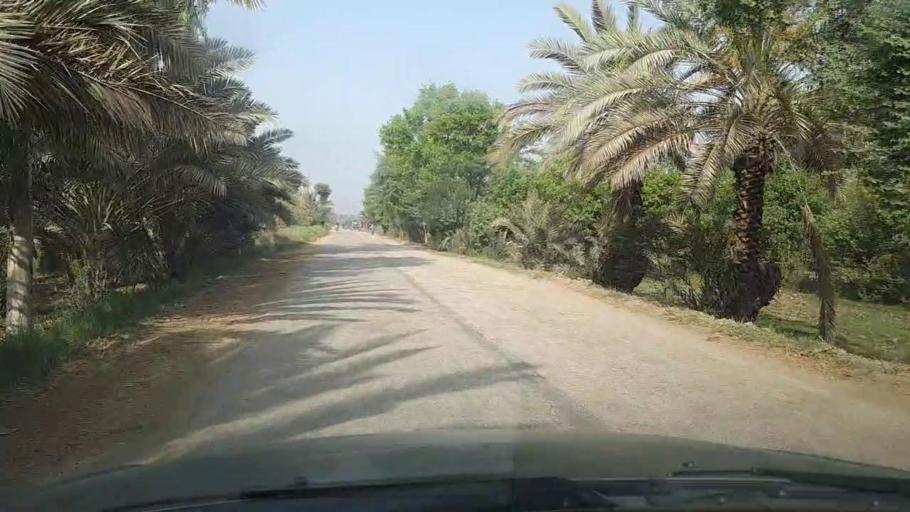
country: PK
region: Sindh
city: Pir jo Goth
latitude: 27.5561
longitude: 68.5447
